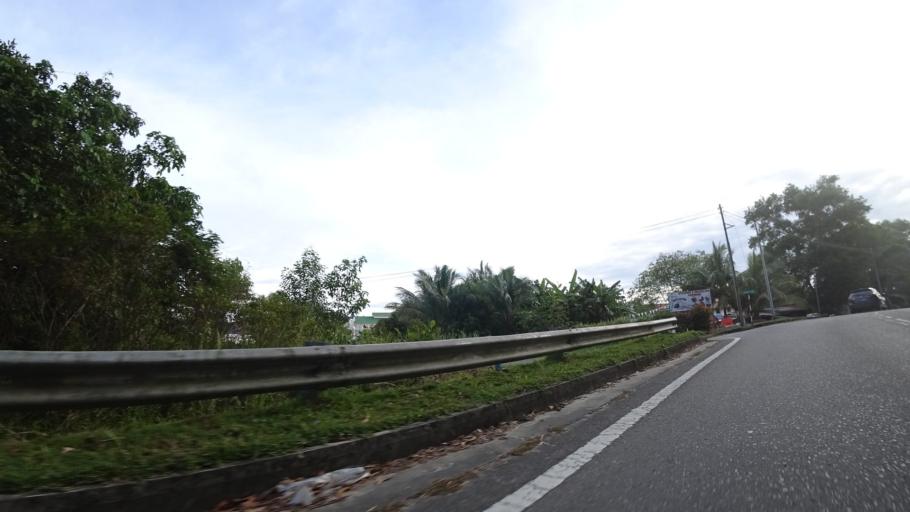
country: BN
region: Brunei and Muara
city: Bandar Seri Begawan
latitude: 4.8898
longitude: 114.9088
